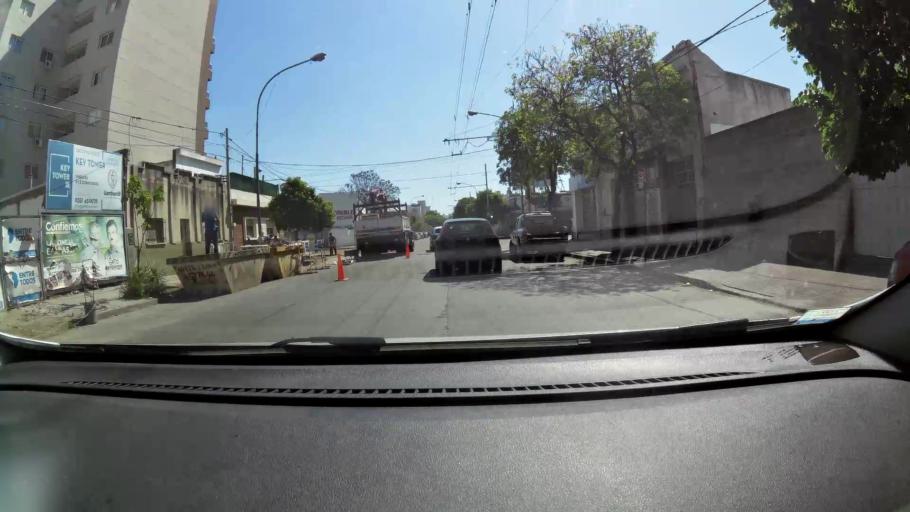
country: AR
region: Cordoba
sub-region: Departamento de Capital
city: Cordoba
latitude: -31.4105
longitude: -64.1668
